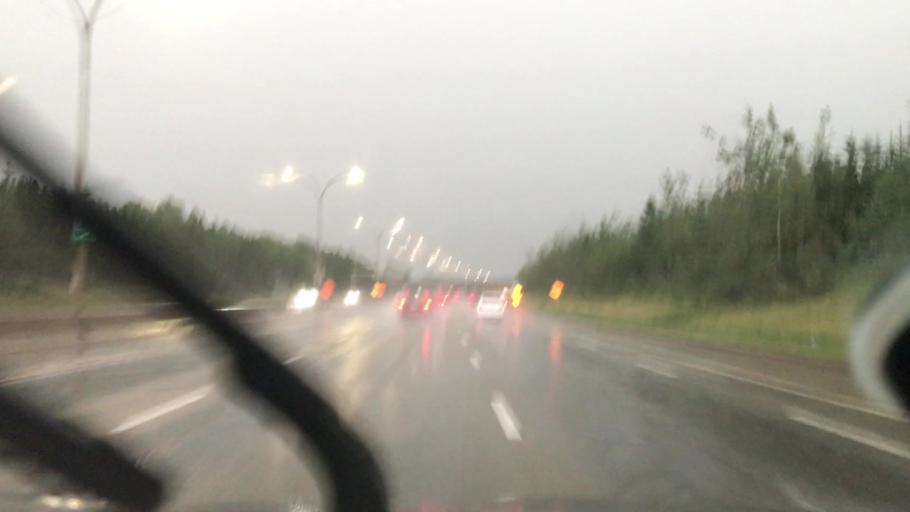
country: CA
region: Alberta
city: Edmonton
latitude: 53.4842
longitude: -113.4585
